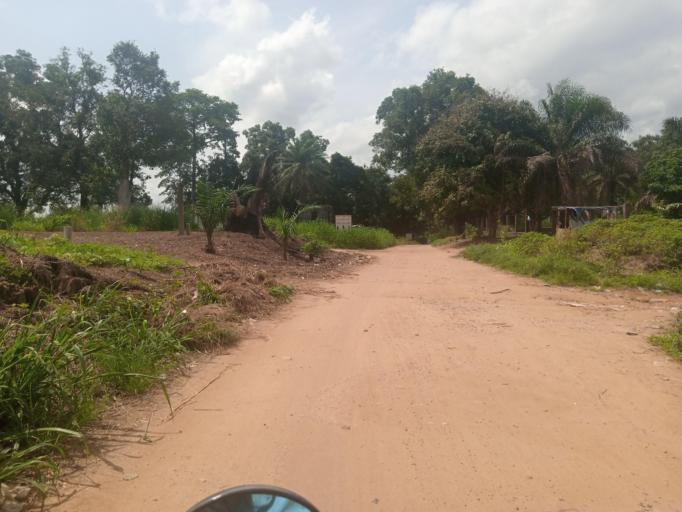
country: SL
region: Southern Province
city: Bo
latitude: 7.9655
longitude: -11.7560
